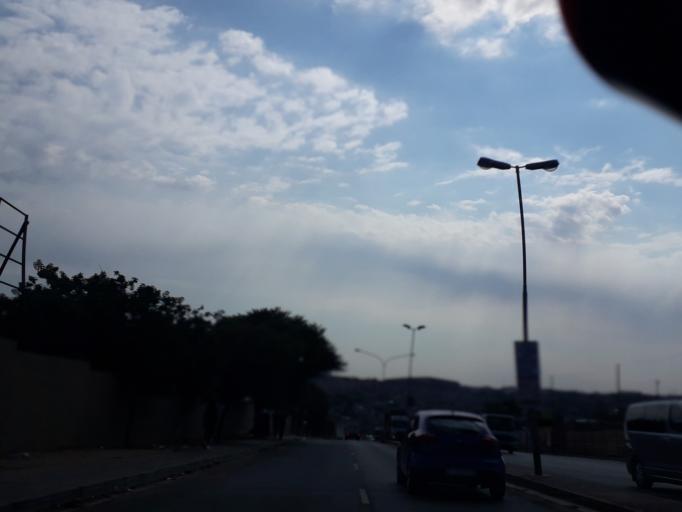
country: ZA
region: Gauteng
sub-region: City of Johannesburg Metropolitan Municipality
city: Modderfontein
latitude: -26.1118
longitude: 28.1064
